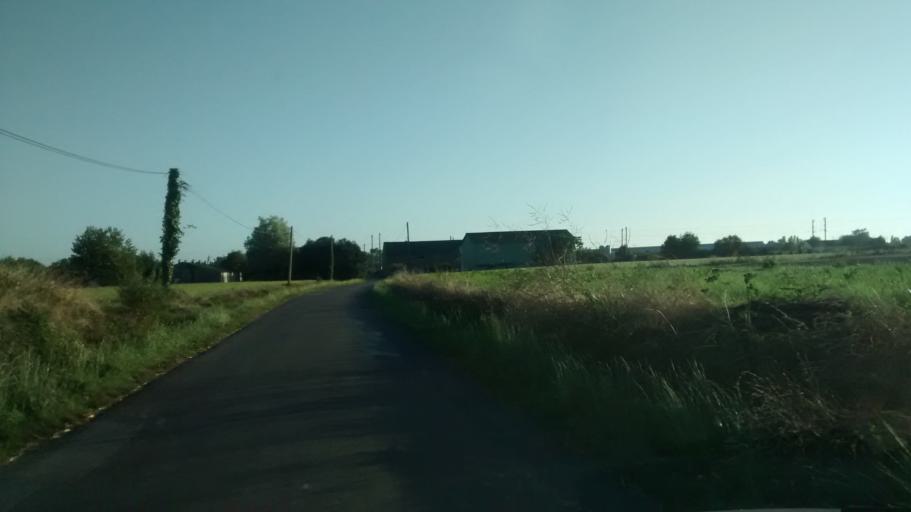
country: FR
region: Brittany
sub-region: Departement d'Ille-et-Vilaine
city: La Fresnais
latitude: 48.5962
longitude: -1.8557
